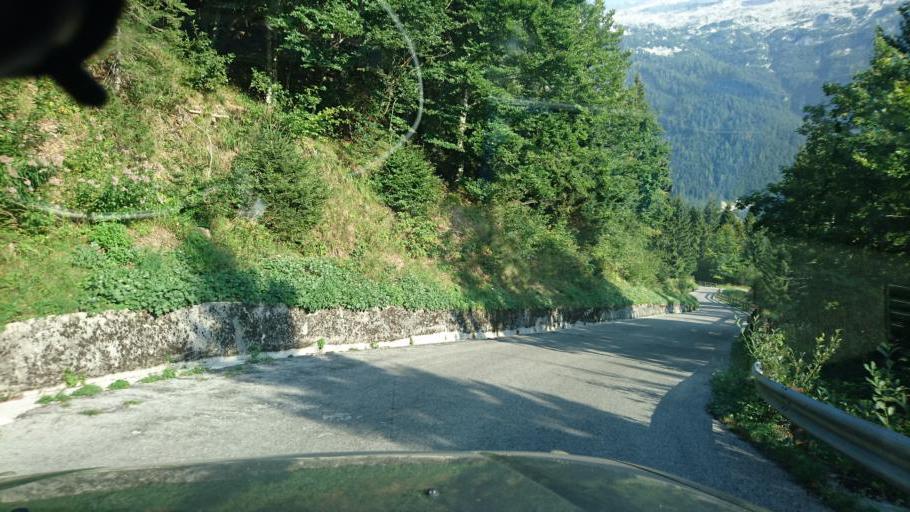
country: SI
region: Bovec
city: Bovec
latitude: 46.3962
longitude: 13.4645
